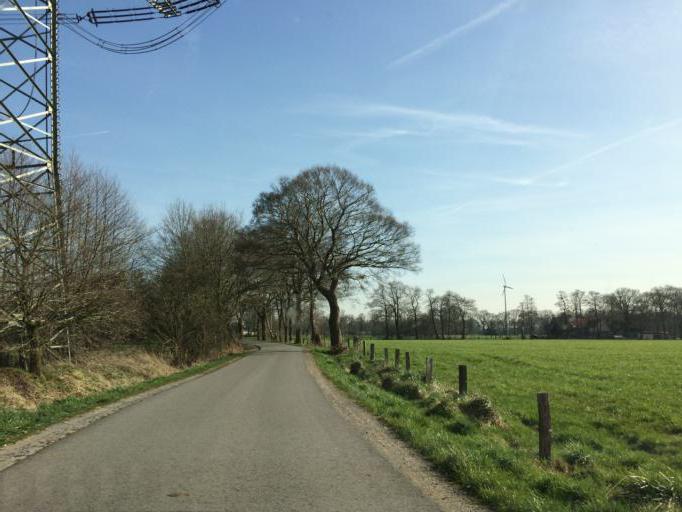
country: DE
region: North Rhine-Westphalia
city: Marl
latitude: 51.6960
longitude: 7.0350
